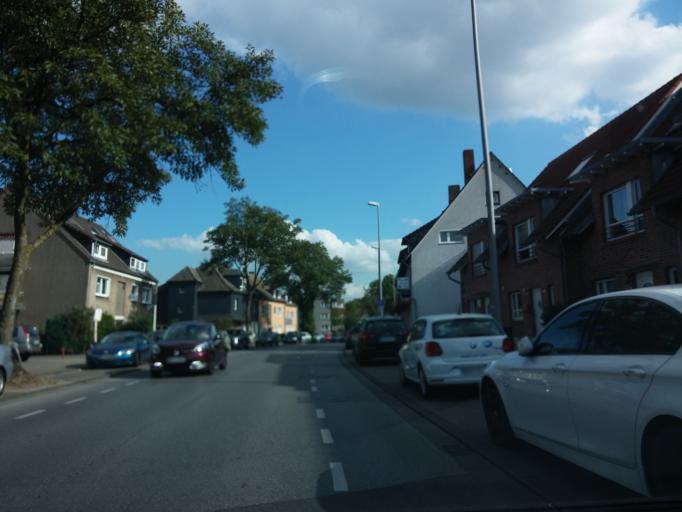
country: DE
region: North Rhine-Westphalia
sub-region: Regierungsbezirk Munster
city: Gladbeck
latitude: 51.5932
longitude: 6.9972
